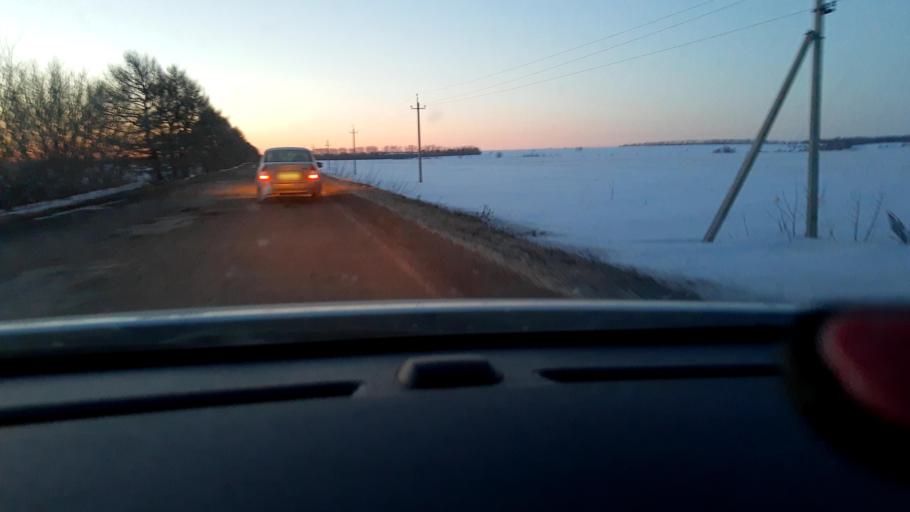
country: RU
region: Bashkortostan
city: Avdon
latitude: 54.3940
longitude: 55.7079
